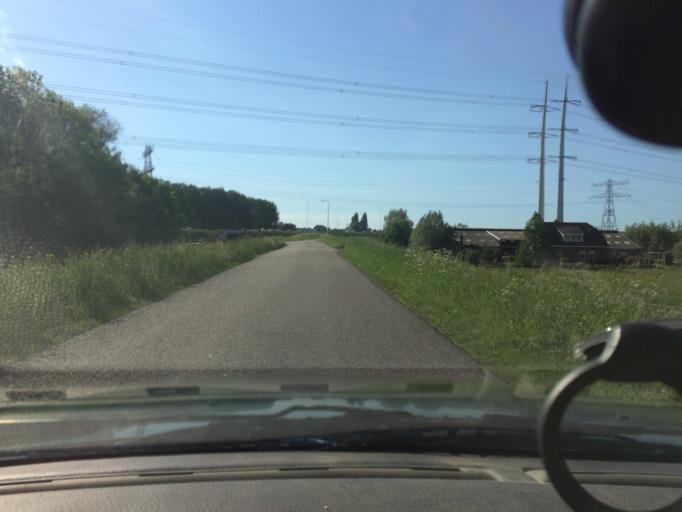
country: NL
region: North Holland
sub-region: Gemeente Haarlem
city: Haarlem
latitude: 52.4046
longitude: 4.7069
